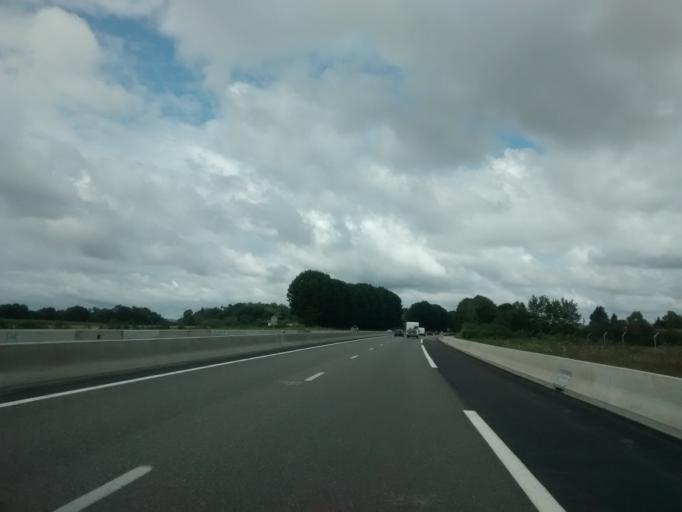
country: FR
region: Aquitaine
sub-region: Departement des Pyrenees-Atlantiques
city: Artix
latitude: 43.3865
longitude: -0.5312
